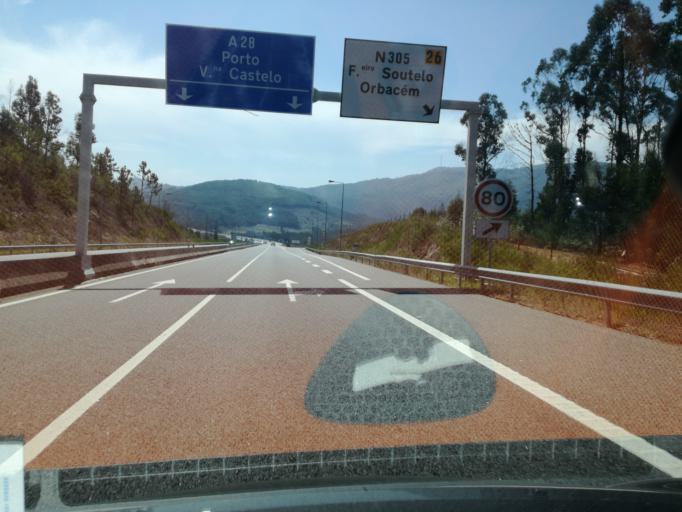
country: PT
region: Viana do Castelo
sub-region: Caminha
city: Vila Praia de Ancora
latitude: 41.8093
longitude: -8.8047
